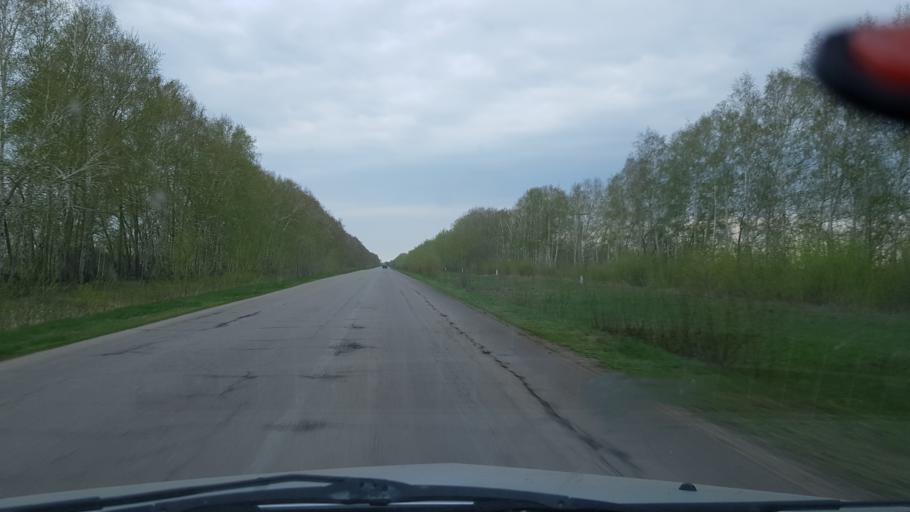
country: RU
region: Samara
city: Podstepki
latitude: 53.6619
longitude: 49.2054
